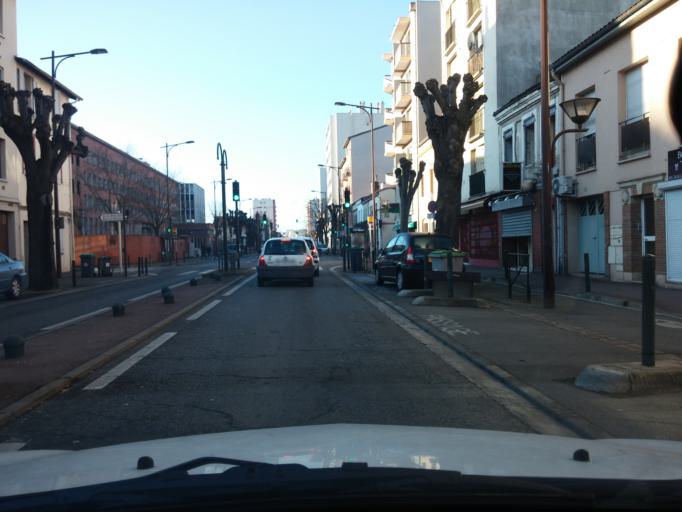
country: FR
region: Midi-Pyrenees
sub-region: Departement de la Haute-Garonne
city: Toulouse
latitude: 43.5824
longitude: 1.4260
